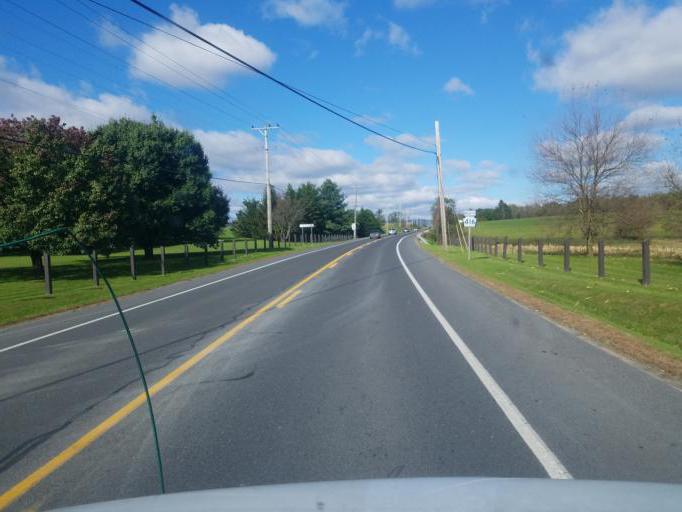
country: US
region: Pennsylvania
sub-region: Franklin County
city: Mercersburg
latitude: 39.8051
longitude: -77.8728
